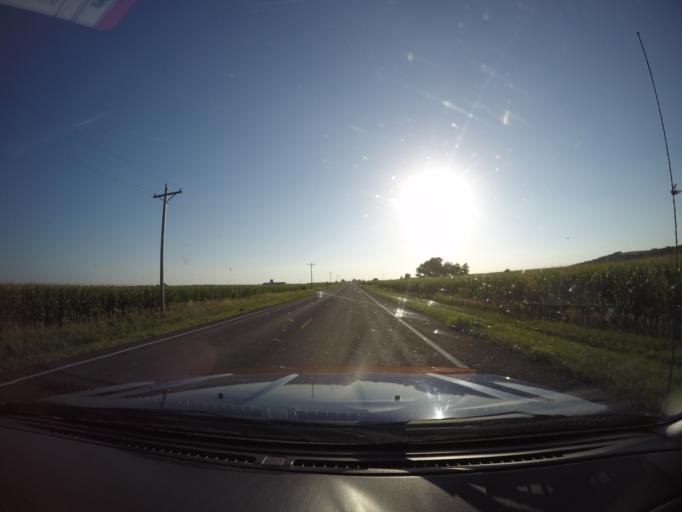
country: US
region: Kansas
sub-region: Pottawatomie County
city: Saint Marys
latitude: 39.2167
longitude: -96.1343
